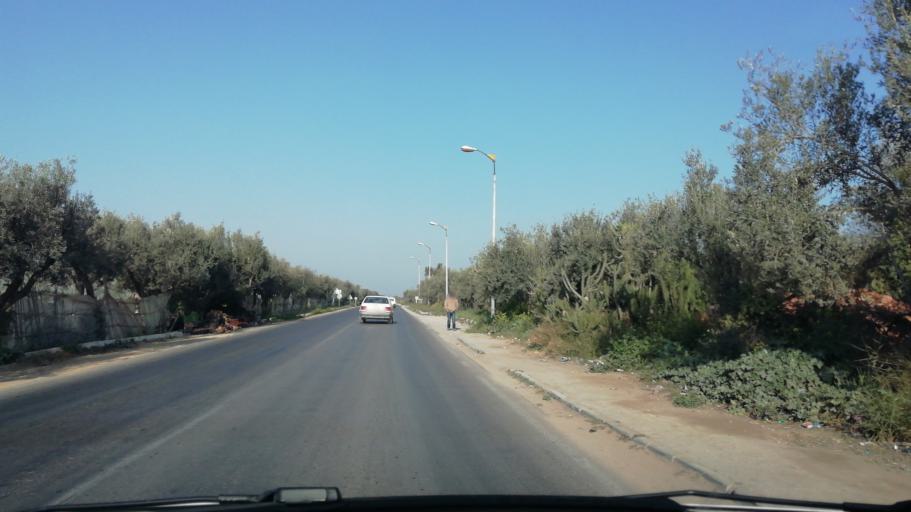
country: DZ
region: Mostaganem
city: Mostaganem
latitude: 35.7536
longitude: 0.1169
